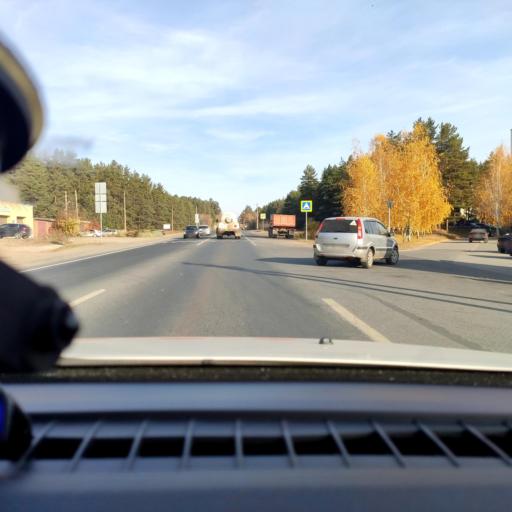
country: RU
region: Samara
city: Volzhskiy
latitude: 53.4385
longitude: 50.1244
